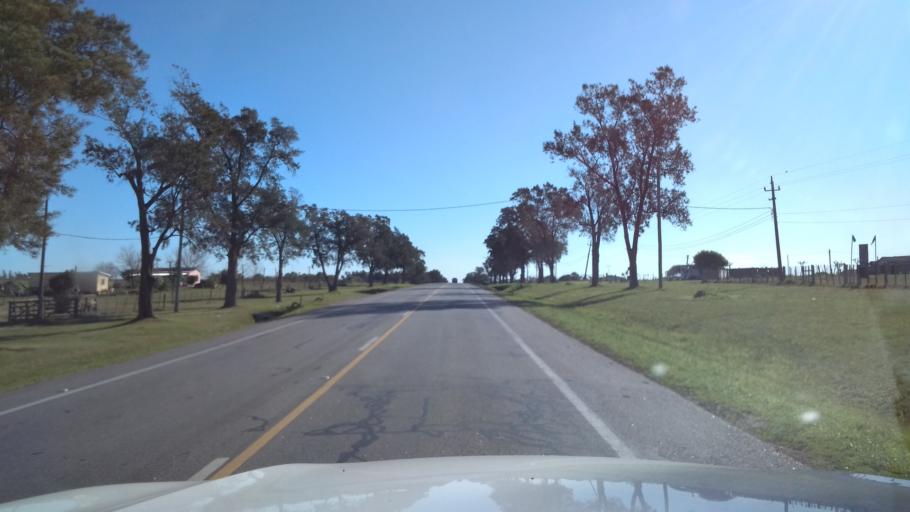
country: UY
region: Canelones
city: San Jacinto
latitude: -34.5396
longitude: -55.8985
